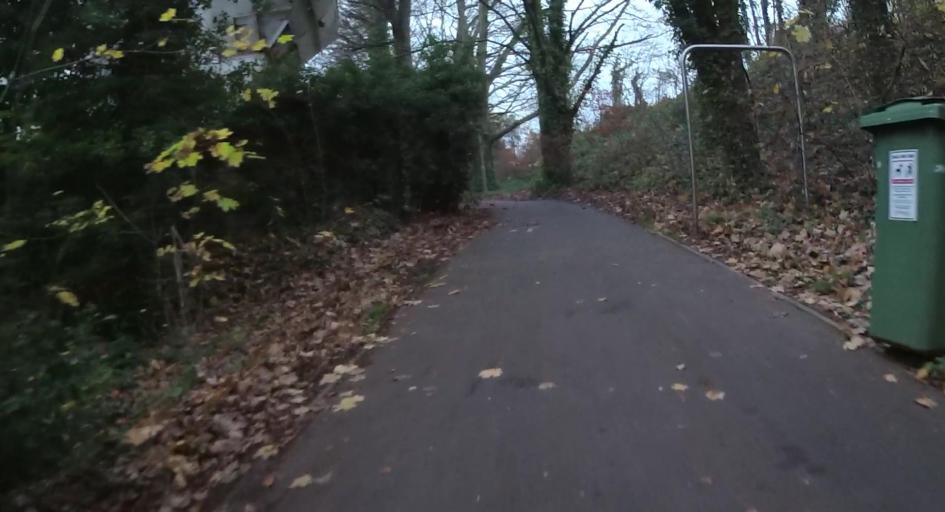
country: GB
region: England
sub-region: Hampshire
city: Kings Worthy
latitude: 51.0683
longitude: -1.2945
